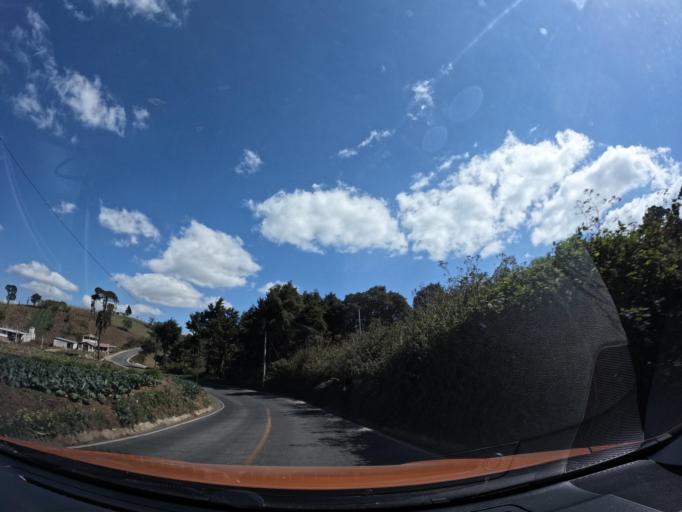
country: GT
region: Chimaltenango
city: Patzun
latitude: 14.6536
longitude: -91.0516
